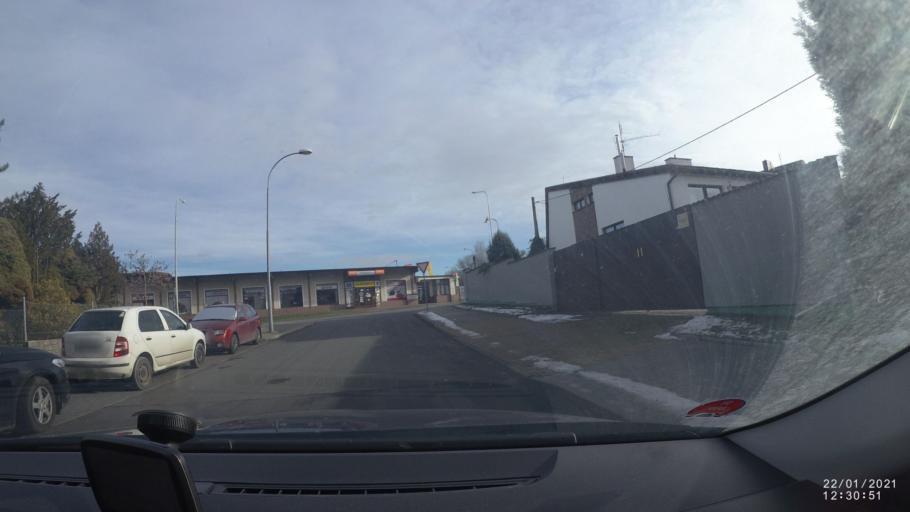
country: CZ
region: Plzensky
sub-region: Okres Plzen-Mesto
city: Pilsen
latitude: 49.7531
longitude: 13.4271
